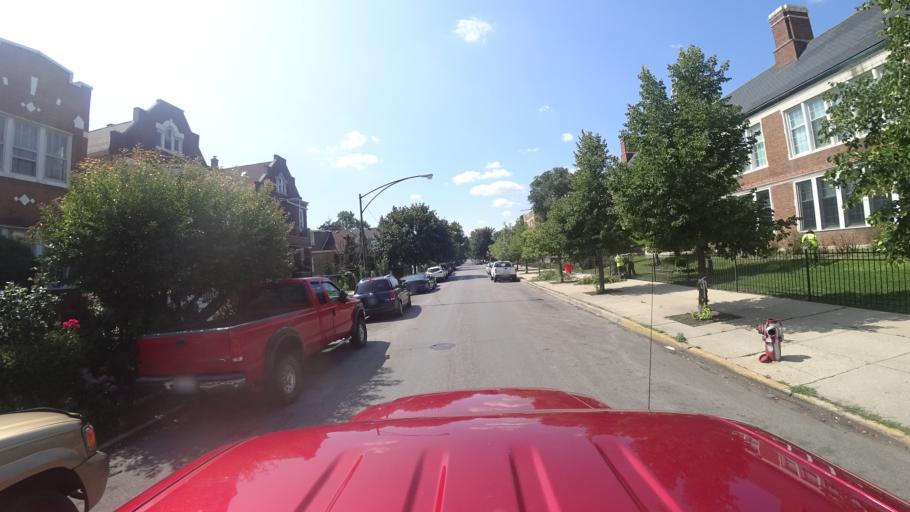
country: US
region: Illinois
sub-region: Cook County
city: Chicago
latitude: 41.7984
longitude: -87.6891
